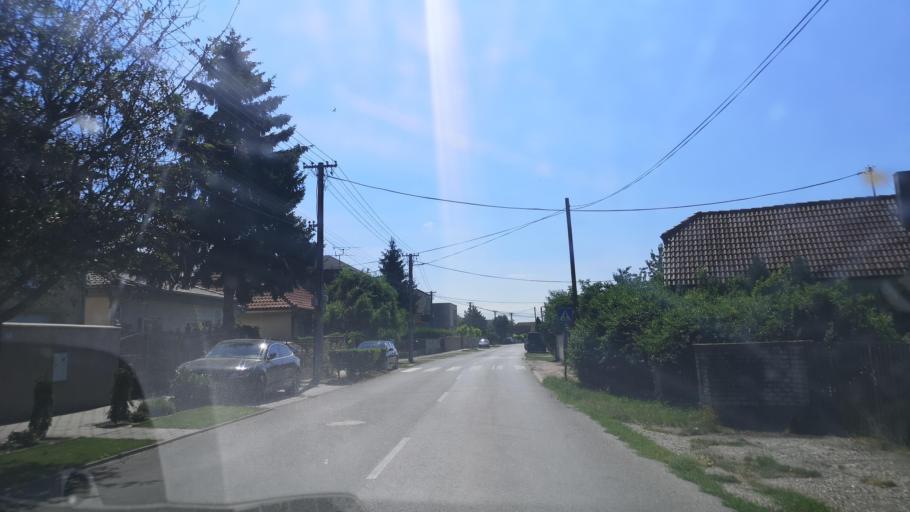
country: SK
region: Bratislavsky
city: Senec
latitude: 48.1152
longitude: 17.4671
